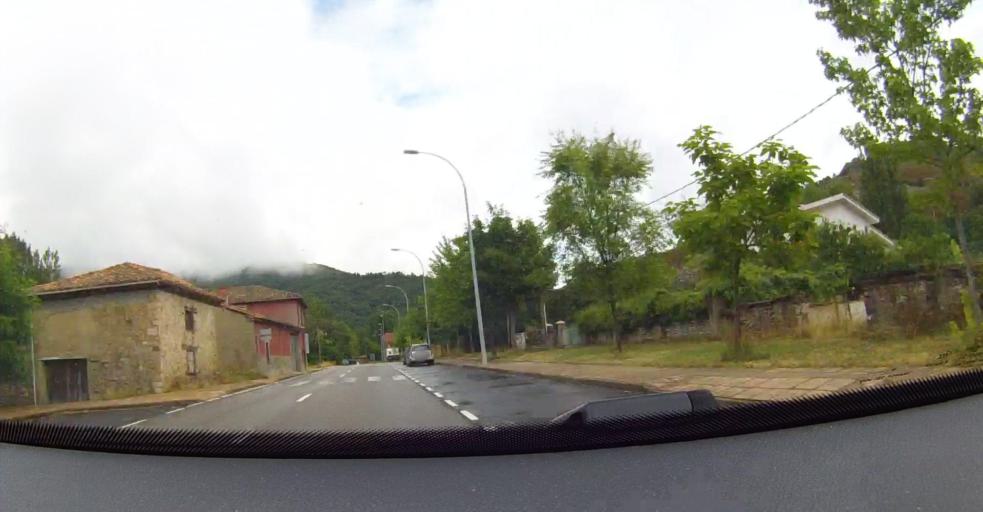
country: ES
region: Castille and Leon
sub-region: Provincia de Leon
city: Bonar
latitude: 42.8746
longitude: -5.3206
